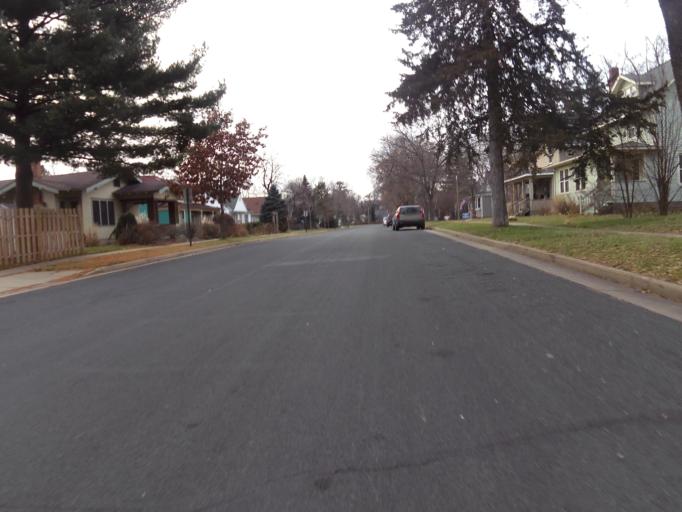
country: US
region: Wisconsin
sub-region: Pierce County
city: River Falls
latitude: 44.8572
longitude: -92.6168
